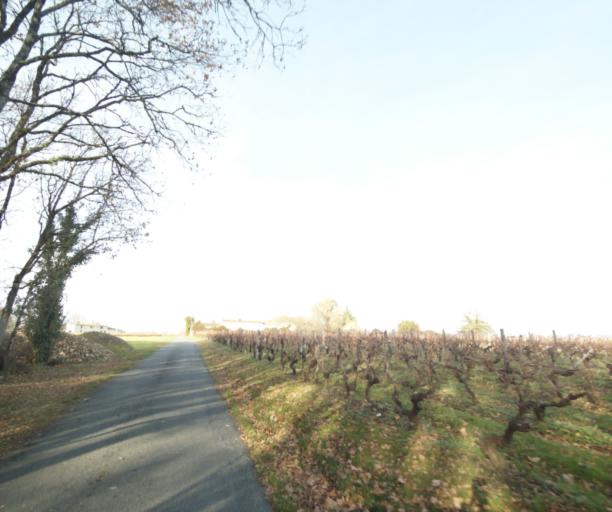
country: FR
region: Poitou-Charentes
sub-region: Departement de la Charente-Maritime
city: Chaniers
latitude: 45.7380
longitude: -0.5125
